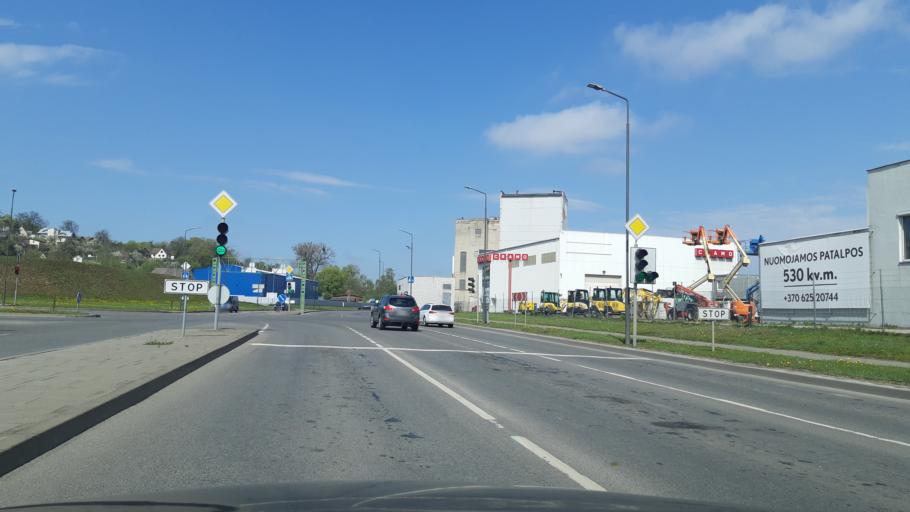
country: LT
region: Kauno apskritis
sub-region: Kaunas
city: Aleksotas
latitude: 54.8819
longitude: 23.9215
